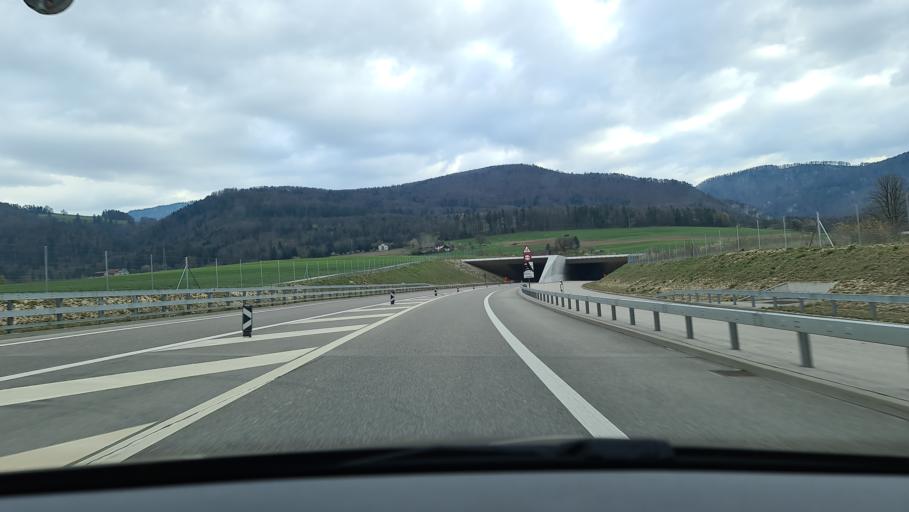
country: CH
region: Jura
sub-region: Delemont District
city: Courrendlin
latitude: 47.3461
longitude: 7.3813
